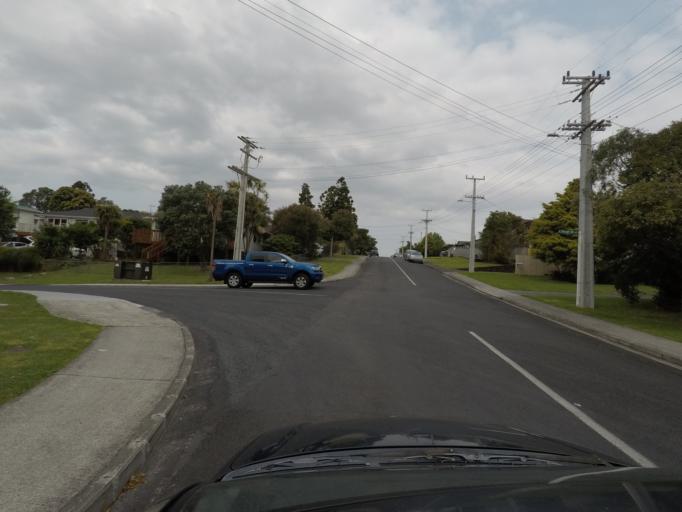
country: NZ
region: Auckland
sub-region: Auckland
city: Rosebank
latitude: -36.8401
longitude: 174.6354
